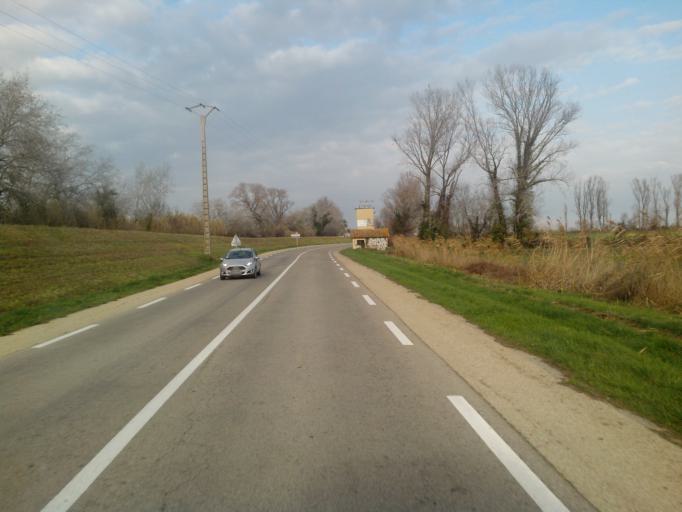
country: FR
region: Languedoc-Roussillon
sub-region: Departement du Gard
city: Saint-Gilles
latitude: 43.6045
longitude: 4.4755
